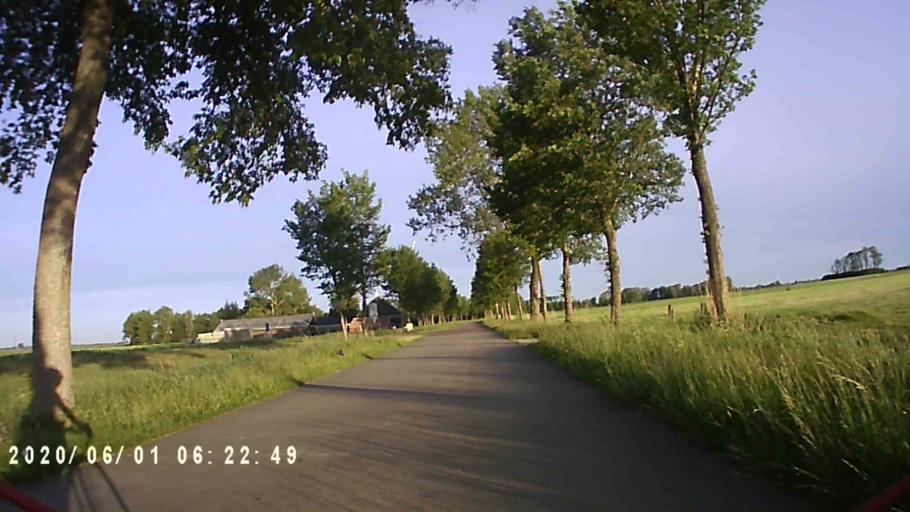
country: NL
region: Friesland
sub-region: Gemeente Kollumerland en Nieuwkruisland
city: Kollum
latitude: 53.2652
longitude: 6.2201
